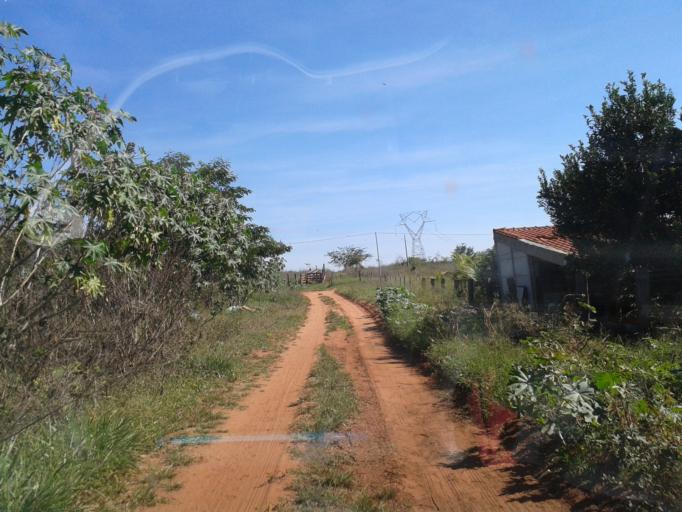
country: BR
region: Minas Gerais
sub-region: Santa Vitoria
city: Santa Vitoria
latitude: -19.0067
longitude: -50.3266
